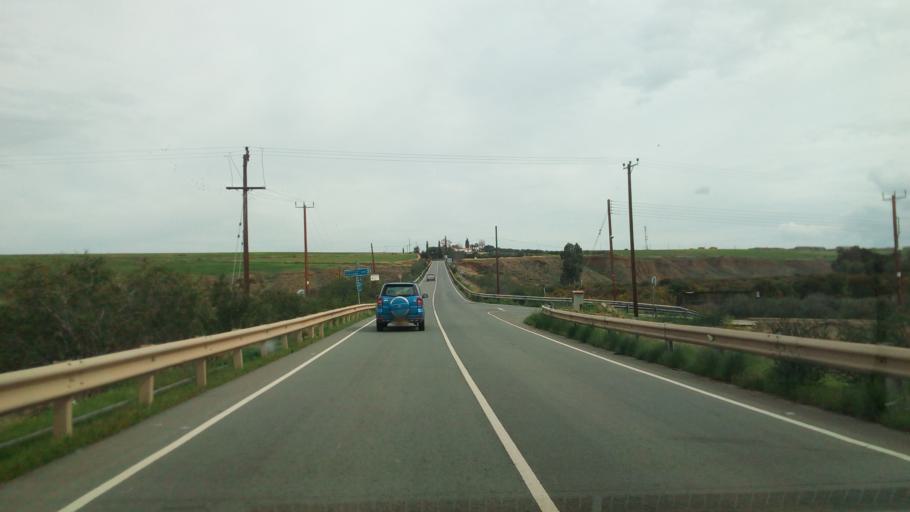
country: CY
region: Lefkosia
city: Astromeritis
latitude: 35.1060
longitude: 32.9752
